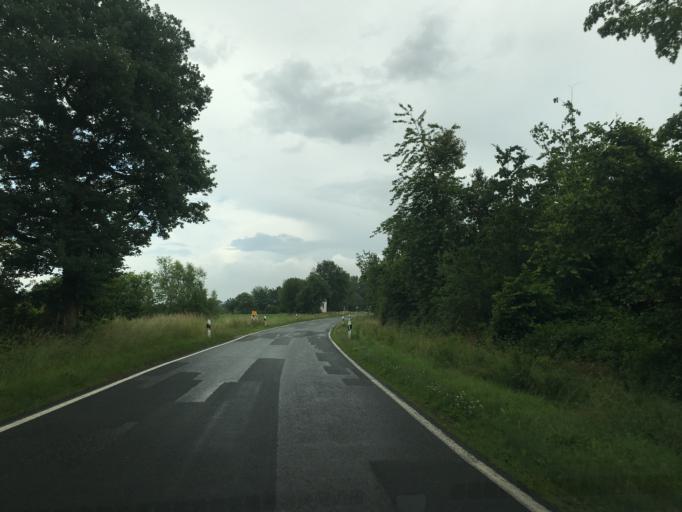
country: DE
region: North Rhine-Westphalia
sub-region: Regierungsbezirk Munster
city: Altenberge
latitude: 52.0123
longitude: 7.4783
